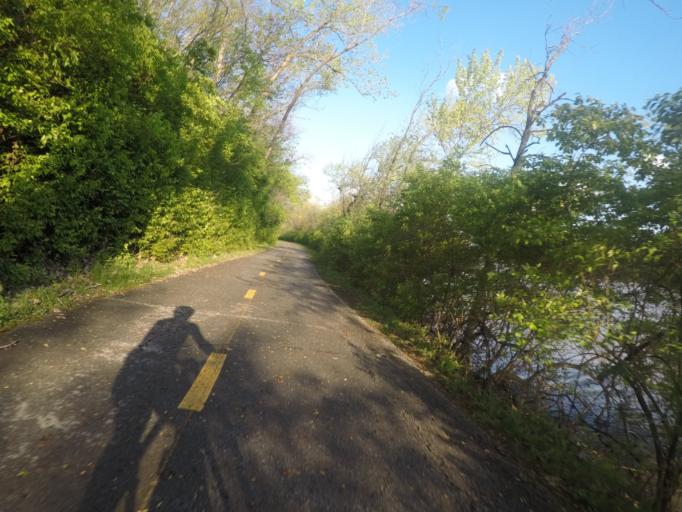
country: US
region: Ohio
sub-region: Franklin County
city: Columbus
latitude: 39.9446
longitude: -83.0071
